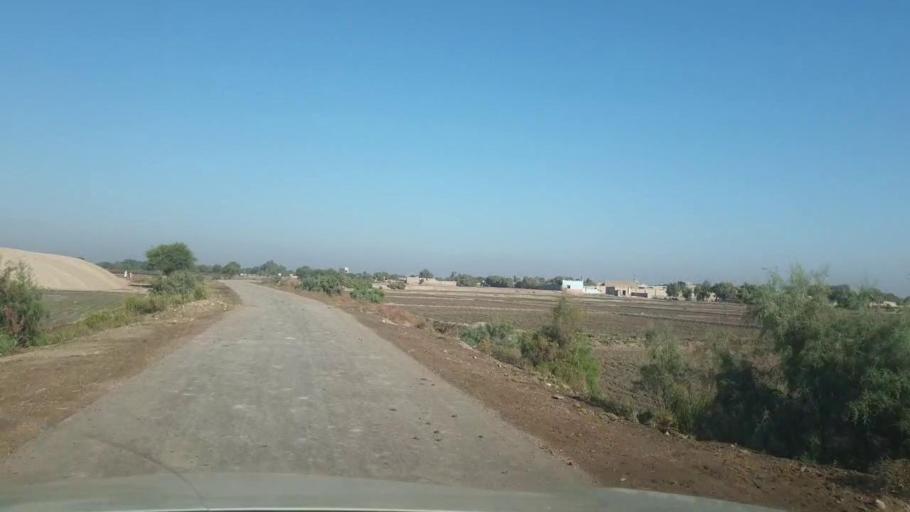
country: PK
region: Sindh
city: Bhan
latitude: 26.5328
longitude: 67.6743
